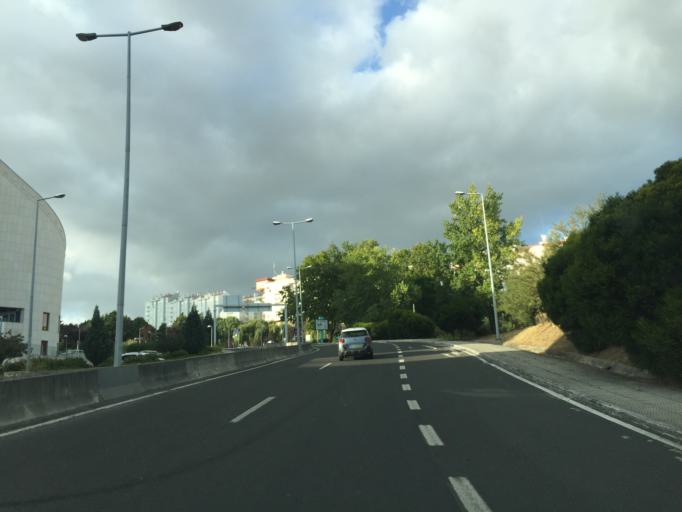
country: PT
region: Lisbon
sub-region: Odivelas
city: Ramada
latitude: 38.8029
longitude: -9.1864
